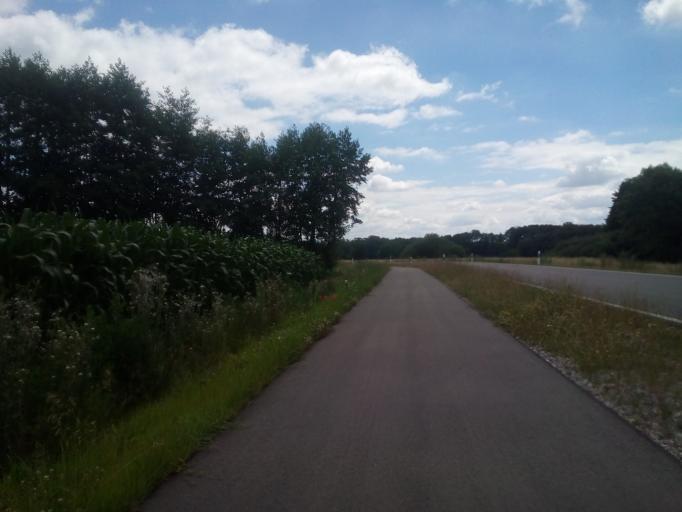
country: DE
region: Baden-Wuerttemberg
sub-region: Freiburg Region
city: Rheinau
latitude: 48.6408
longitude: 7.9390
